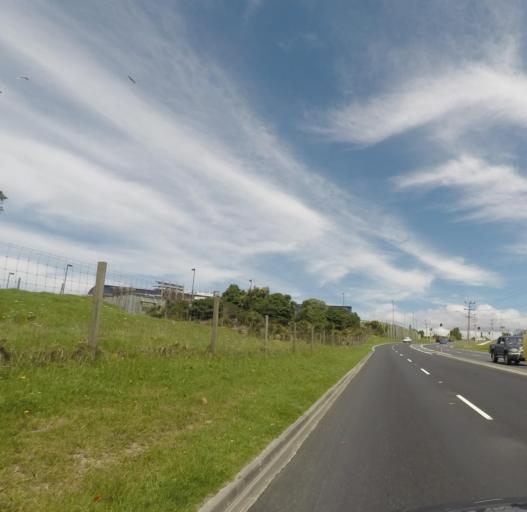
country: NZ
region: Auckland
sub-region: Auckland
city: Rothesay Bay
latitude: -36.6231
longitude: 174.6723
